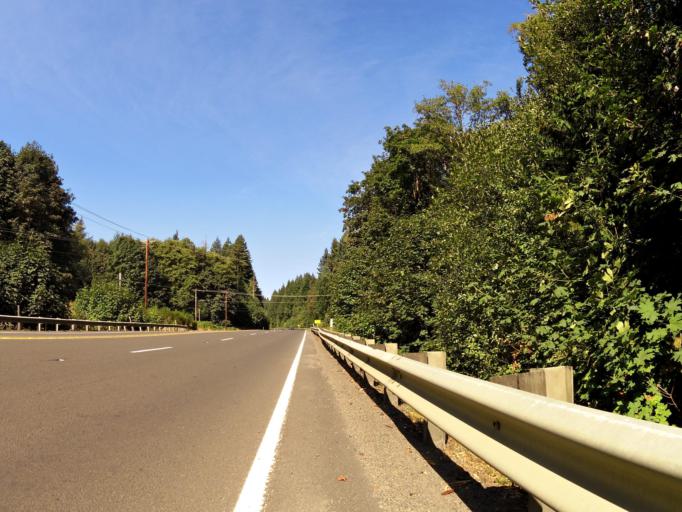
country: US
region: Washington
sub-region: Wahkiakum County
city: Cathlamet
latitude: 46.1520
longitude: -123.4121
